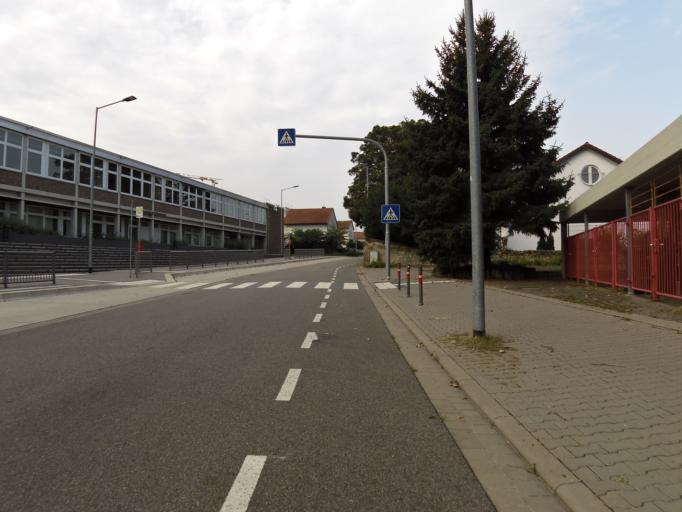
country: DE
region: Rheinland-Pfalz
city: Alzey
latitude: 49.7432
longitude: 8.1169
